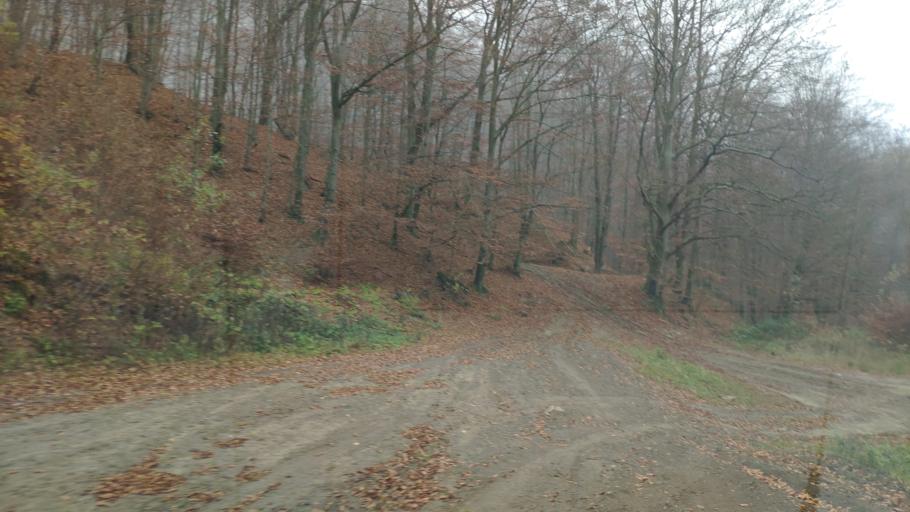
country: SK
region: Presovsky
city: Sabinov
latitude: 49.1582
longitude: 21.2010
